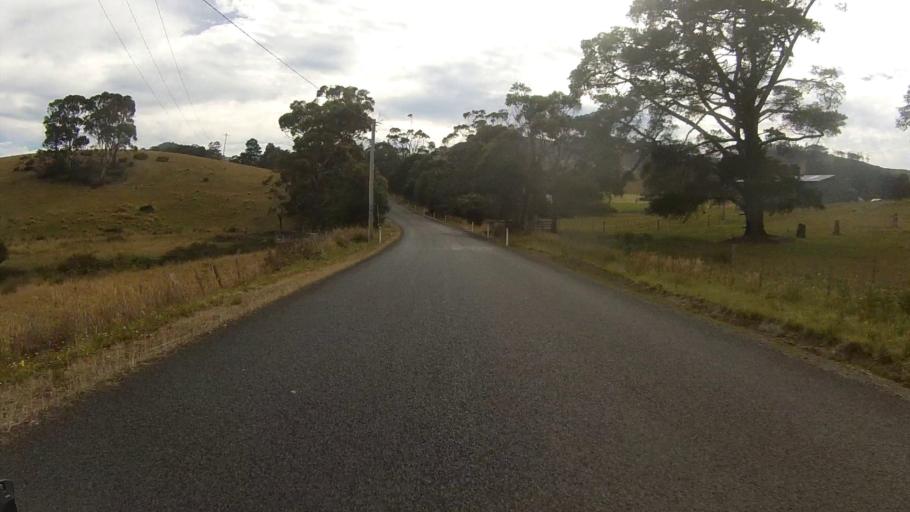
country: AU
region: Tasmania
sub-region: Sorell
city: Sorell
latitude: -42.7889
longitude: 147.8048
